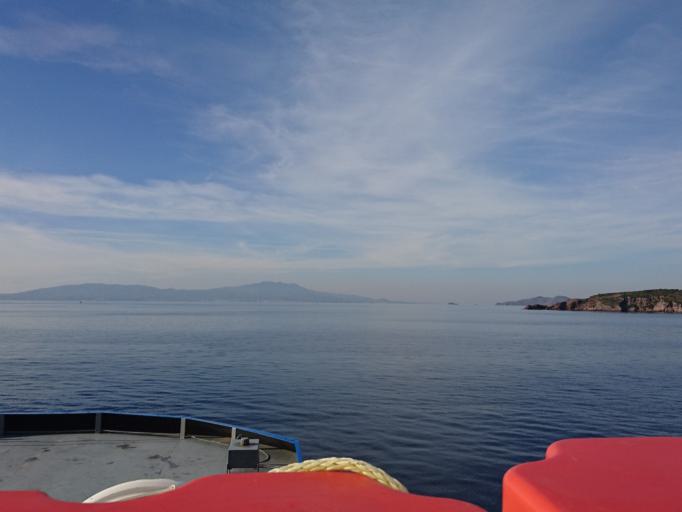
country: TR
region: Mugla
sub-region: Bodrum
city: Bodrum
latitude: 36.9942
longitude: 27.3961
